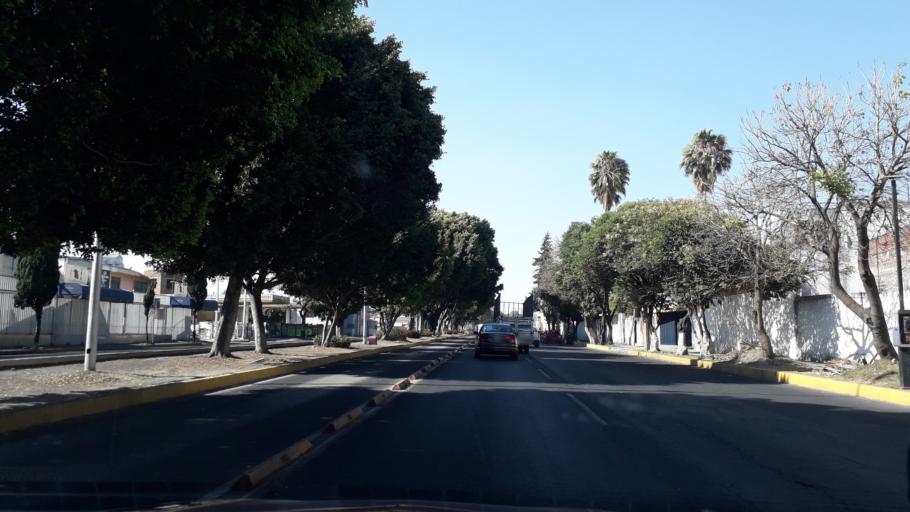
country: MX
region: Puebla
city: Puebla
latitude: 19.0584
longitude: -98.1925
